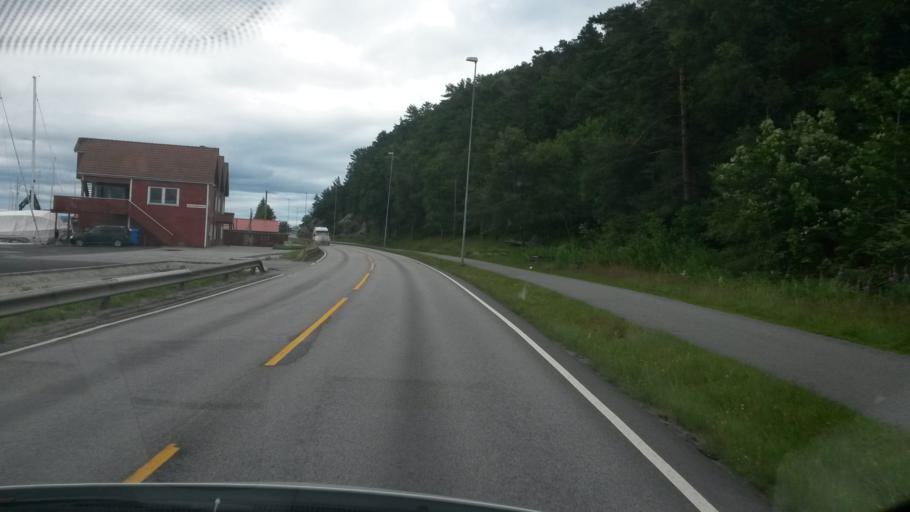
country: NO
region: Rogaland
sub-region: Sandnes
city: Sandnes
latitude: 58.8638
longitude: 5.7556
